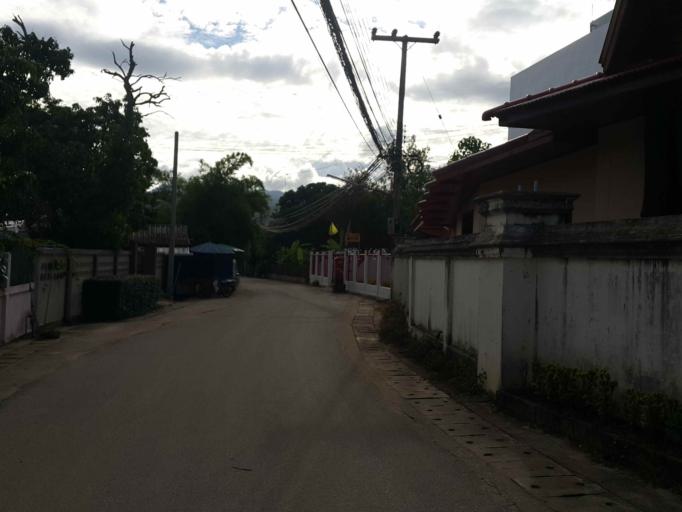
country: TH
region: Chiang Mai
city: Mae Chaem
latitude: 18.4970
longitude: 98.3642
